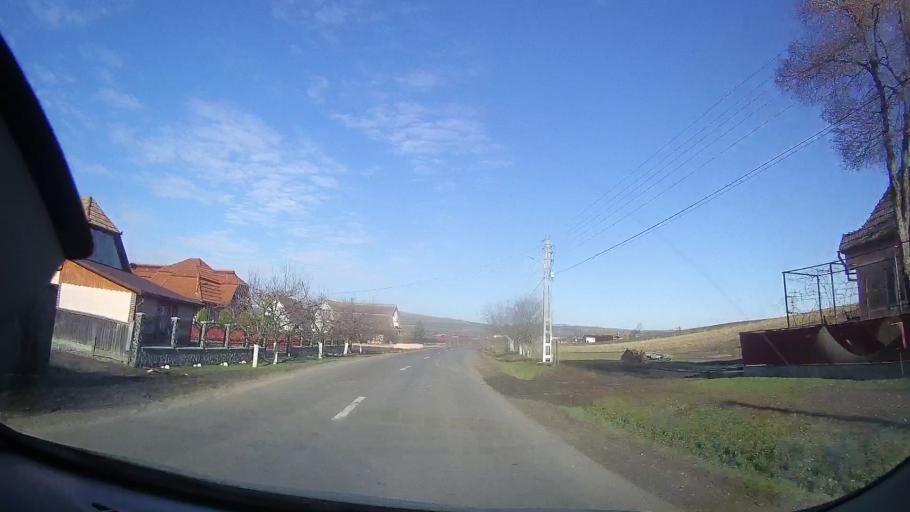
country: RO
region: Mures
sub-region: Comuna Grebenisu de Campie
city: Grebenisu de Campie
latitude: 46.5588
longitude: 24.3346
